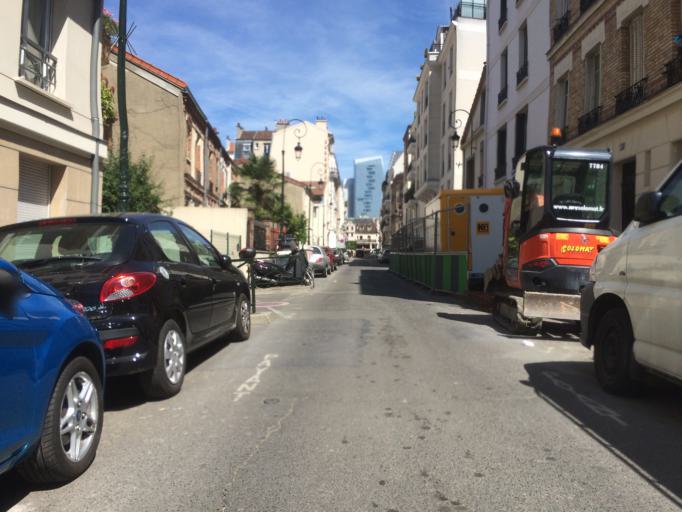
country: FR
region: Ile-de-France
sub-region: Departement des Hauts-de-Seine
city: Puteaux
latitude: 48.8806
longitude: 2.2342
